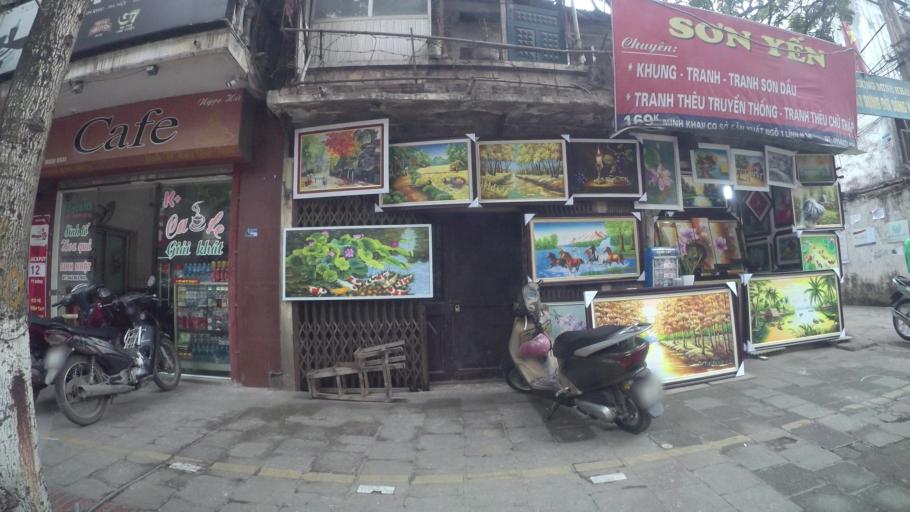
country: VN
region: Ha Noi
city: Hai BaTrung
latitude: 20.9952
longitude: 105.8561
